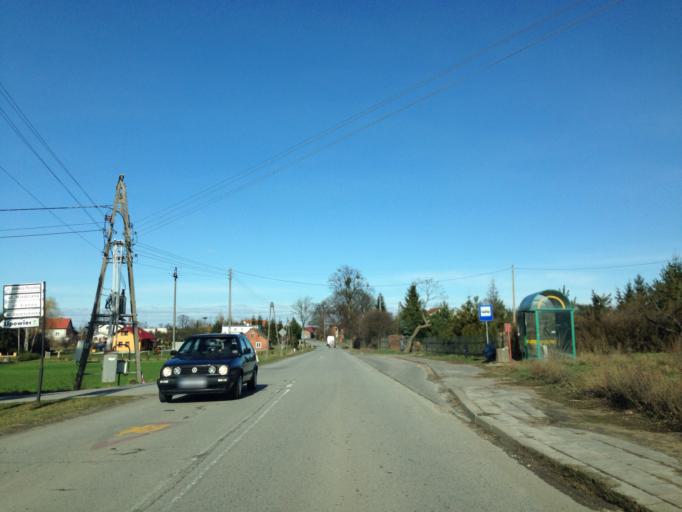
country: PL
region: Pomeranian Voivodeship
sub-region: Powiat malborski
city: Malbork
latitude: 54.0134
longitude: 19.0653
